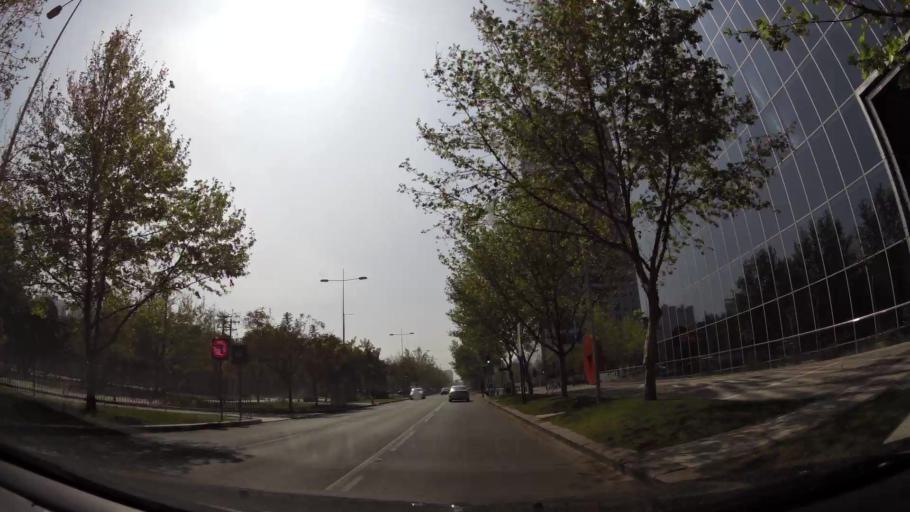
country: CL
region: Santiago Metropolitan
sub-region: Provincia de Santiago
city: Villa Presidente Frei, Nunoa, Santiago, Chile
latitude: -33.4043
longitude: -70.5738
